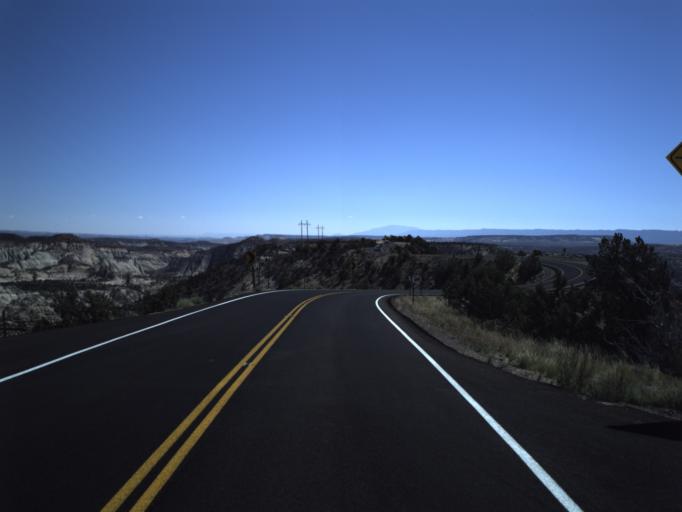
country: US
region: Utah
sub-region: Wayne County
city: Loa
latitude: 37.8395
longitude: -111.4213
